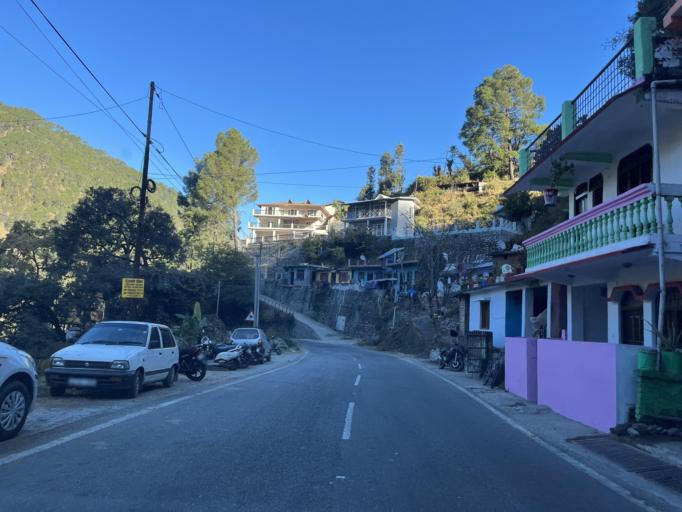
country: IN
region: Uttarakhand
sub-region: Naini Tal
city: Bhowali
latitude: 29.4051
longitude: 79.5153
